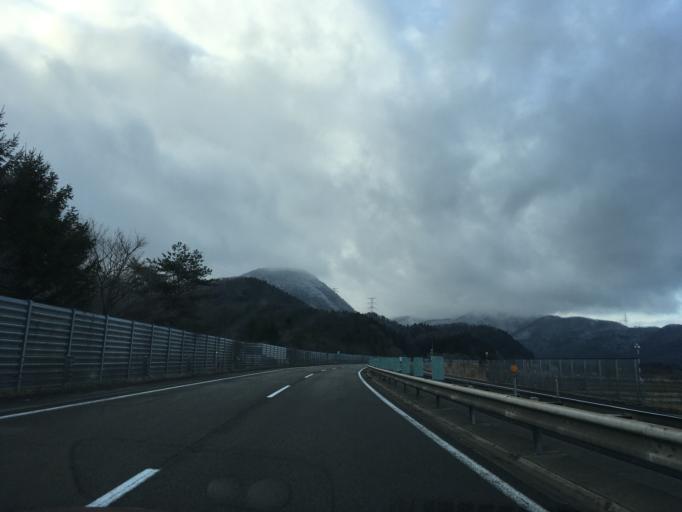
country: JP
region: Miyagi
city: Shiroishi
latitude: 38.1850
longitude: 140.6004
